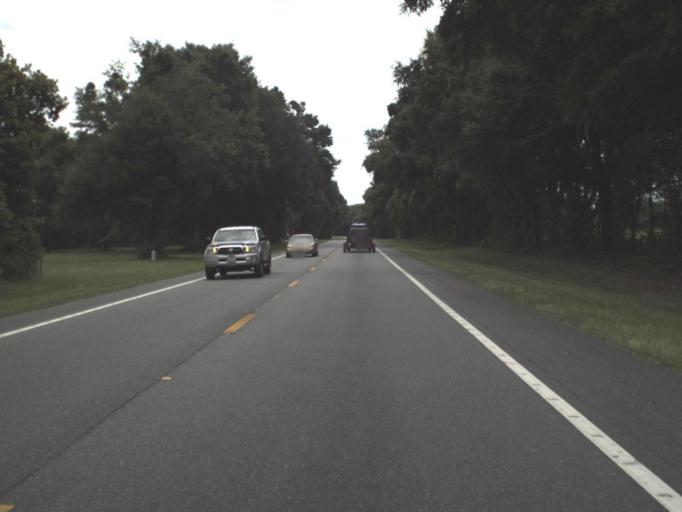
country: US
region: Florida
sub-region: Suwannee County
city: Wellborn
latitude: 29.9697
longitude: -82.8982
